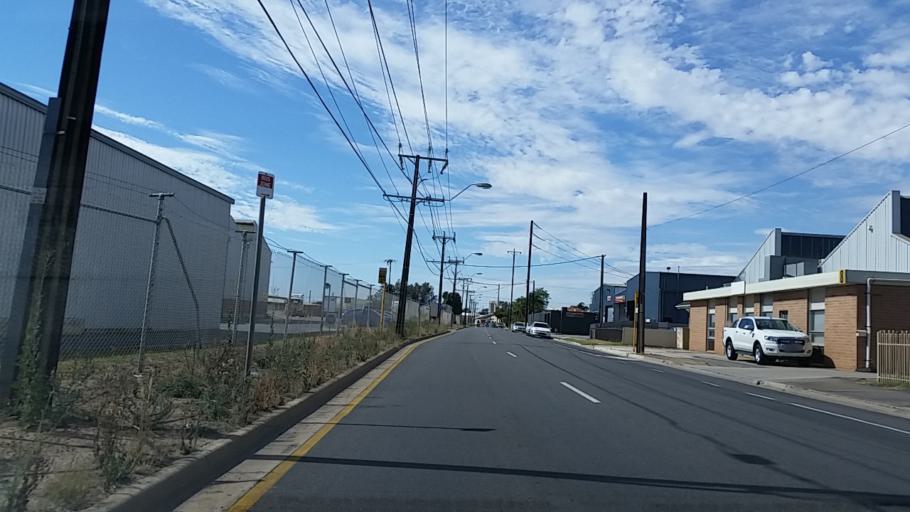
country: AU
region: South Australia
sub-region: Port Adelaide Enfield
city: Alberton
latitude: -34.8544
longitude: 138.5381
